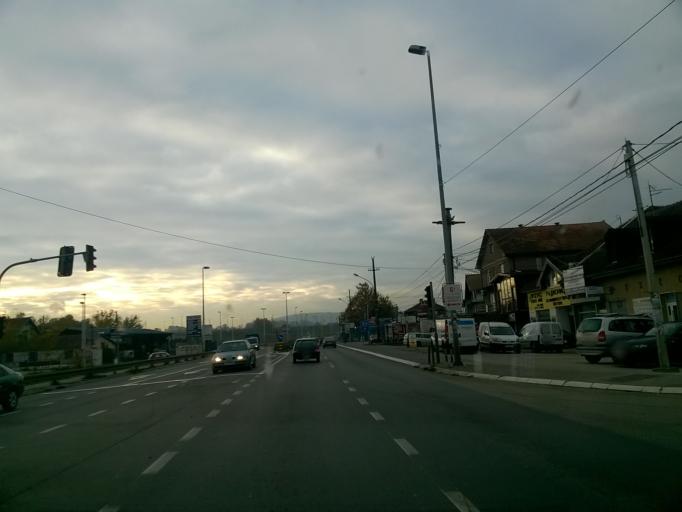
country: RS
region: Central Serbia
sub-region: Belgrade
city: Stari Grad
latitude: 44.8396
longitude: 20.4917
